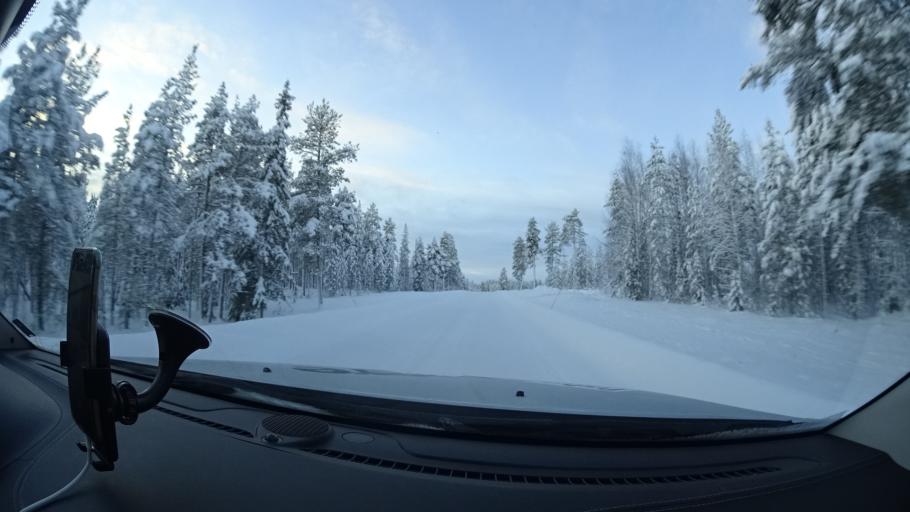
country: SE
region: Norrbotten
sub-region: Jokkmokks Kommun
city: Jokkmokk
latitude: 66.0255
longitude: 19.8898
